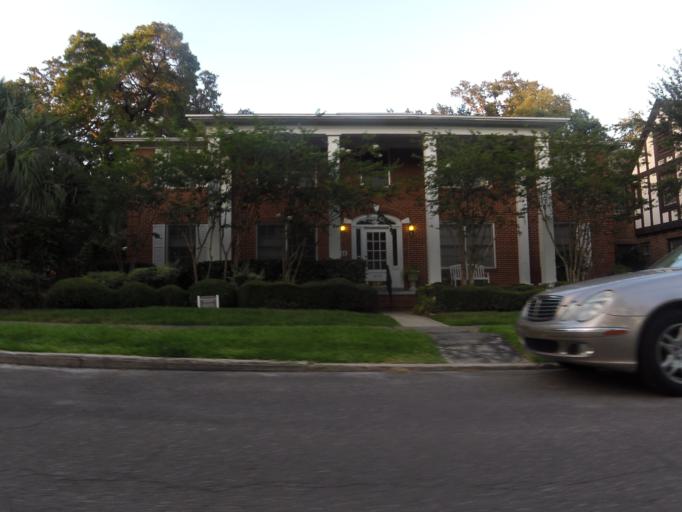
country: US
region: Florida
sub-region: Duval County
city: Jacksonville
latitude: 30.3034
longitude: -81.6952
